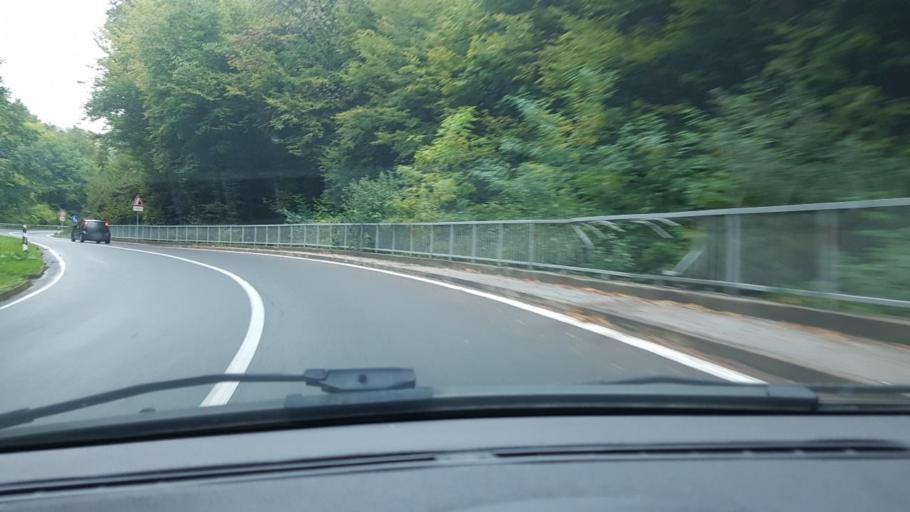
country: HR
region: Krapinsko-Zagorska
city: Marija Bistrica
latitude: 45.9456
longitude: 16.0990
